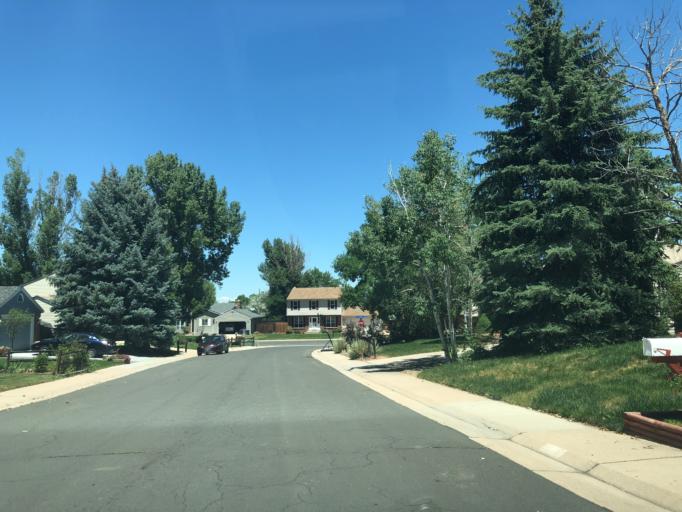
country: US
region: Colorado
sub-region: Arapahoe County
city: Dove Valley
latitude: 39.6207
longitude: -104.7815
